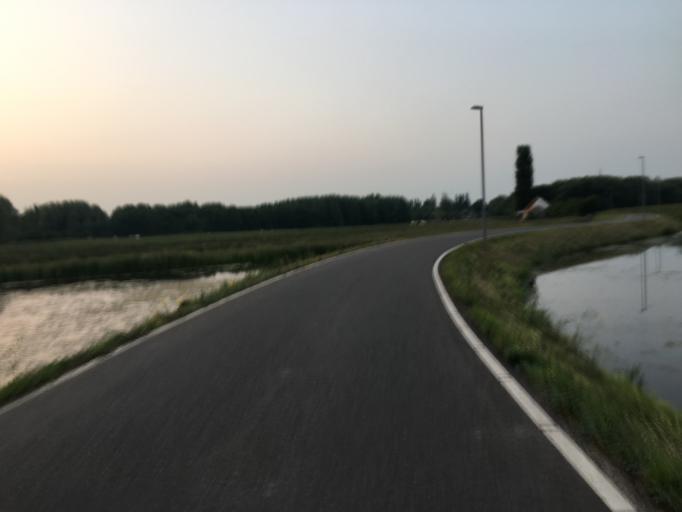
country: NL
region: South Holland
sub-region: Gemeente Schiedam
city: Schiedam
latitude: 51.9522
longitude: 4.3946
